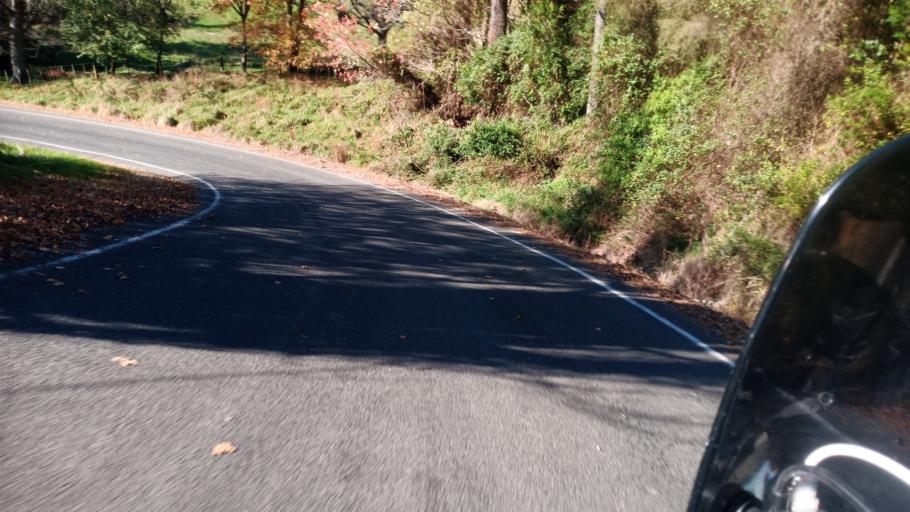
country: NZ
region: Hawke's Bay
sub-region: Wairoa District
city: Wairoa
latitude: -38.8207
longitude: 177.2951
